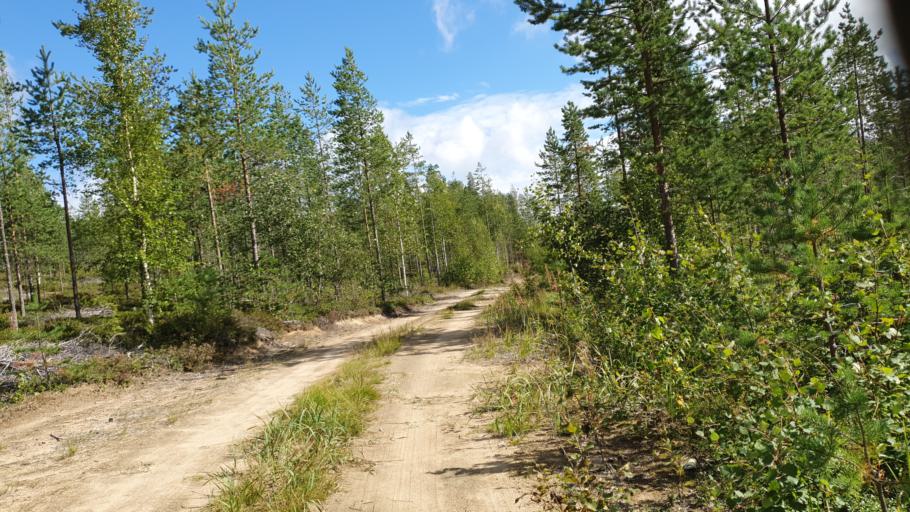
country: FI
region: Kainuu
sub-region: Kehys-Kainuu
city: Kuhmo
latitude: 64.1485
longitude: 29.3650
